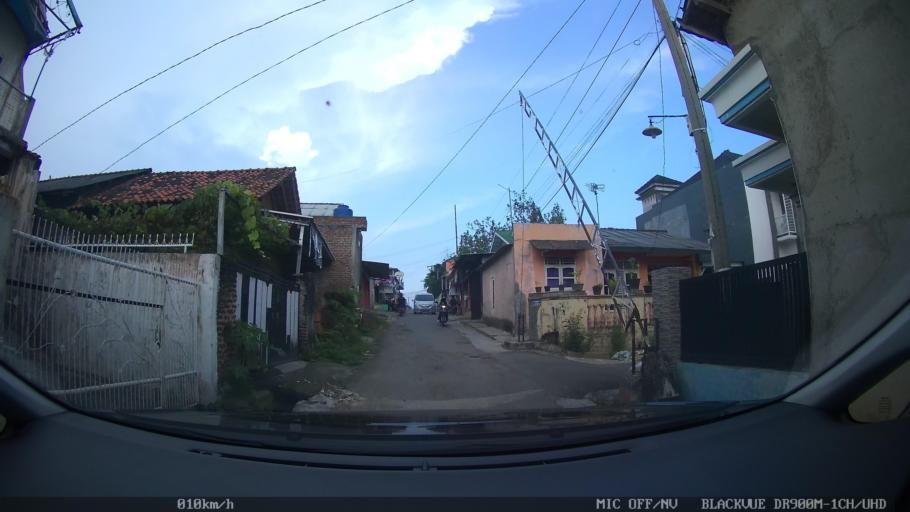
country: ID
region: Lampung
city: Kedaton
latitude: -5.3935
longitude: 105.2009
